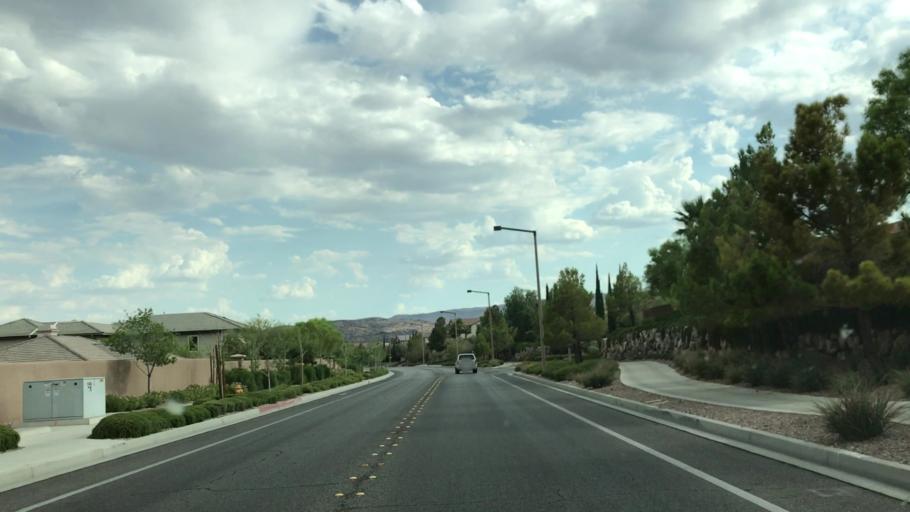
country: US
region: Nevada
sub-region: Clark County
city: Summerlin South
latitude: 36.1759
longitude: -115.3514
